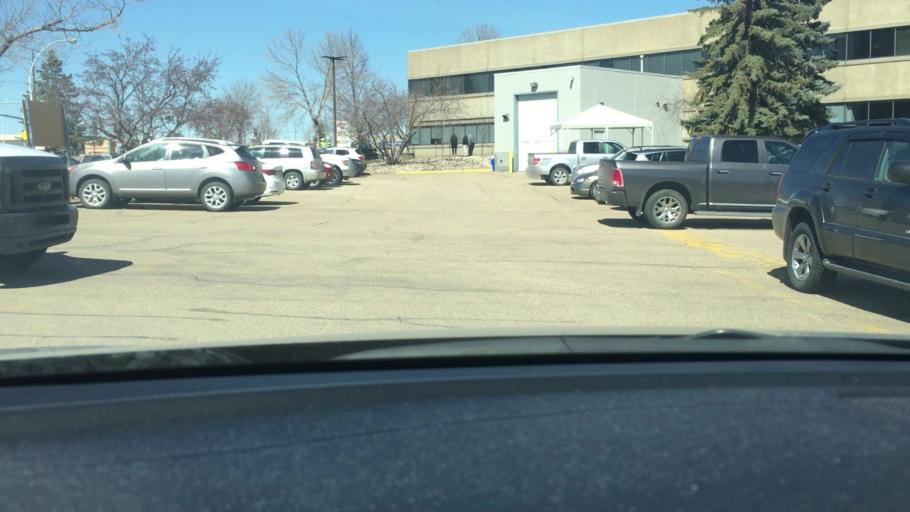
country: CA
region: Alberta
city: Edmonton
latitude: 53.5363
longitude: -113.4178
